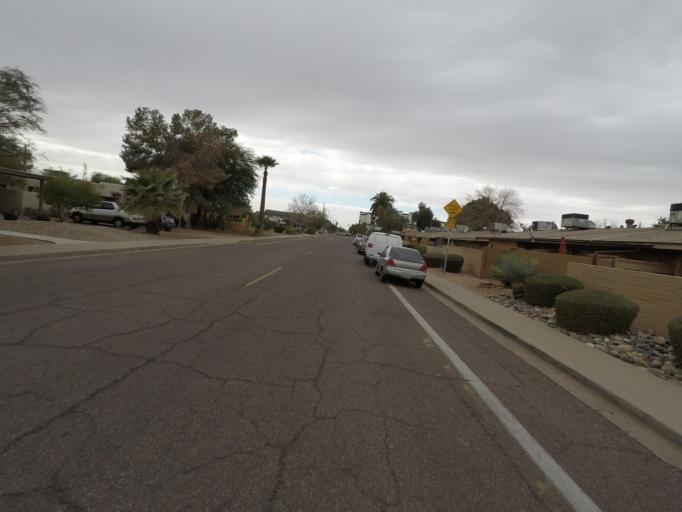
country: US
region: Arizona
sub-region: Maricopa County
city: Phoenix
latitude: 33.5020
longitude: -112.0455
